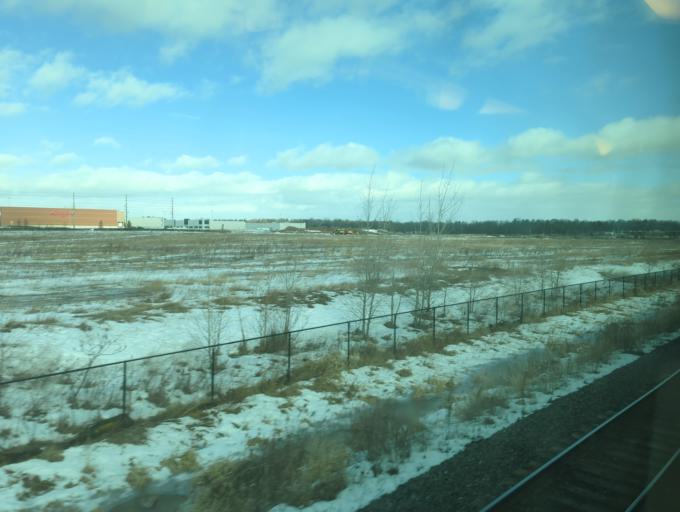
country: CA
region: Ontario
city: Oakville
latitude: 43.3952
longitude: -79.7443
